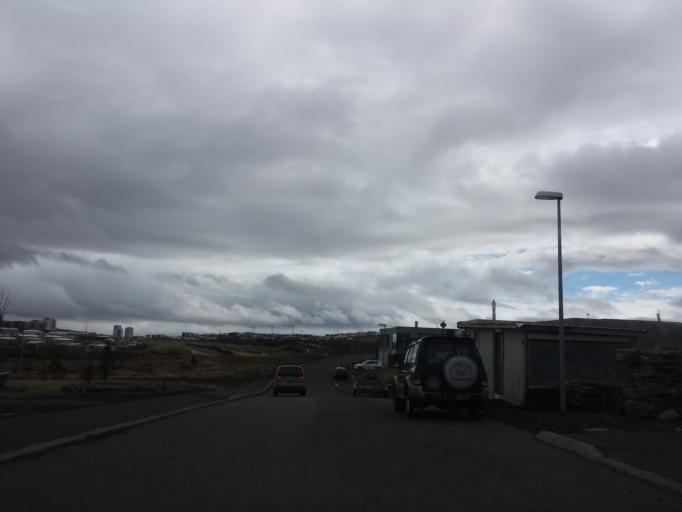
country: IS
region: Capital Region
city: Kopavogur
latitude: 64.0930
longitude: -21.8712
